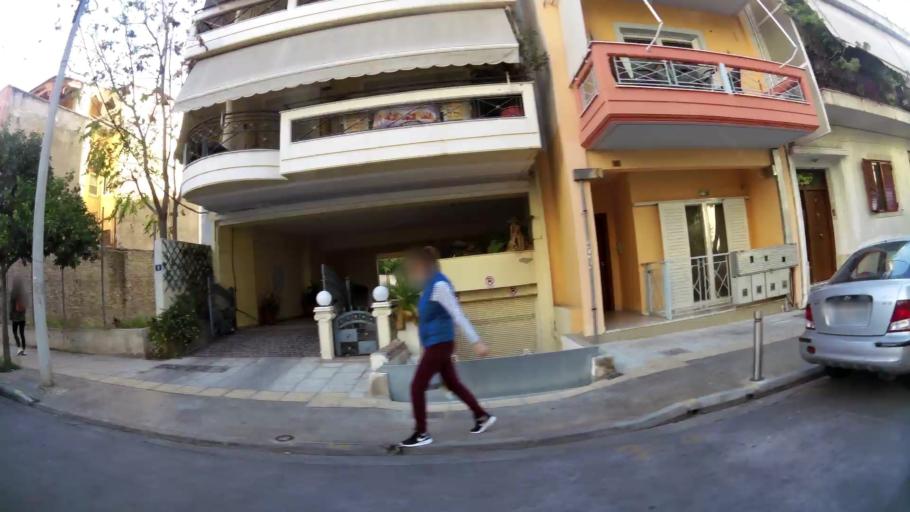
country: GR
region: Attica
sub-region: Nomos Piraios
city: Nikaia
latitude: 37.9742
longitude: 23.6554
